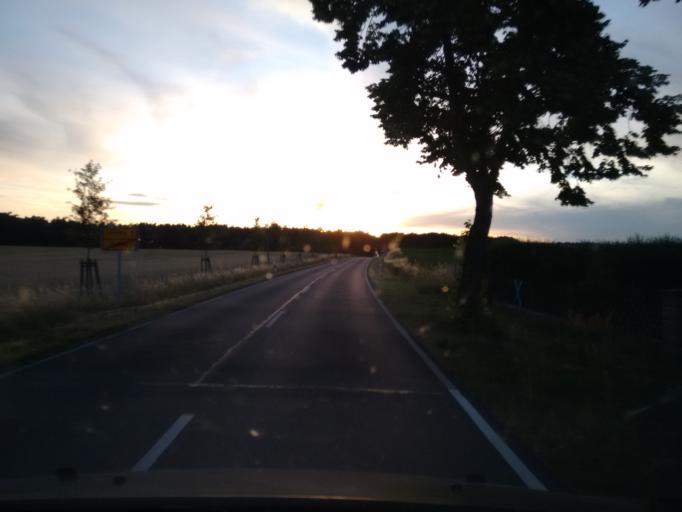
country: DE
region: Brandenburg
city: Tauche
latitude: 52.1870
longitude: 14.1554
